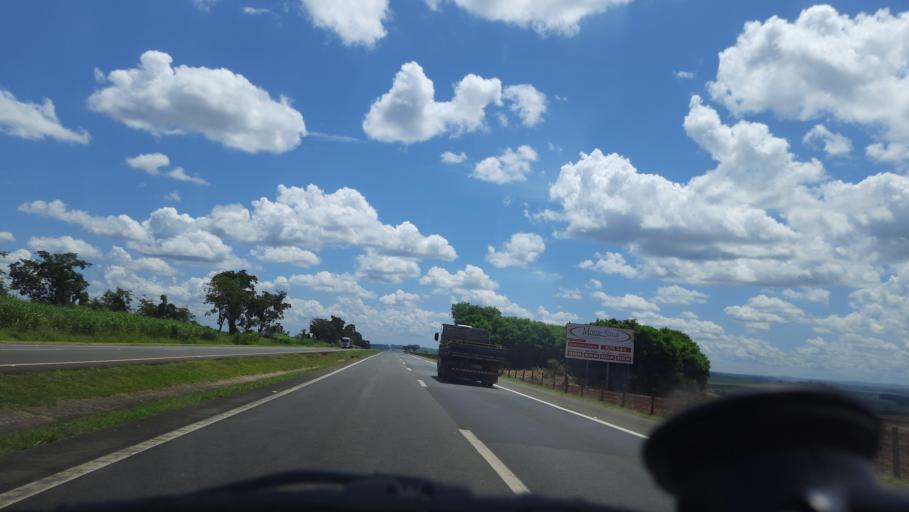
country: BR
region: Sao Paulo
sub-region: Aguai
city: Aguai
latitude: -22.0286
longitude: -47.0332
